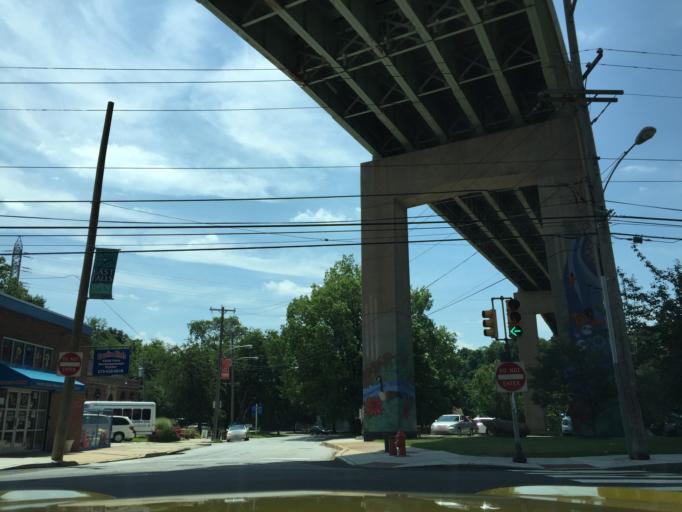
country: US
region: Pennsylvania
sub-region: Montgomery County
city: Bala-Cynwyd
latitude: 40.0080
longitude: -75.1913
